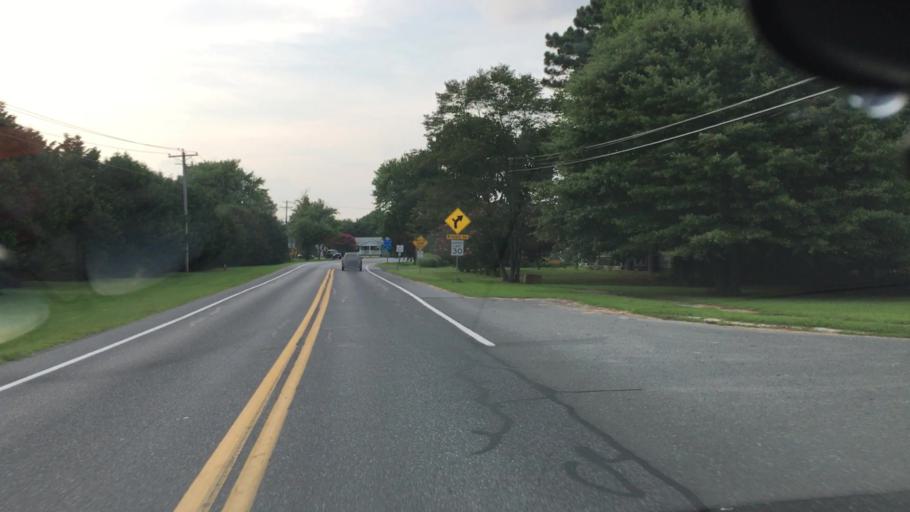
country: US
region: Delaware
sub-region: Sussex County
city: Ocean View
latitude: 38.5361
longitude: -75.0903
